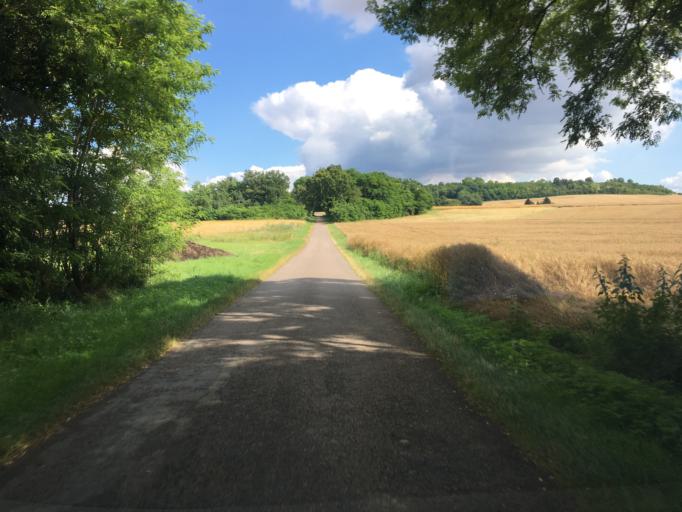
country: FR
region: Bourgogne
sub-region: Departement de l'Yonne
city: Aillant-sur-Tholon
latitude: 47.8275
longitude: 3.3749
